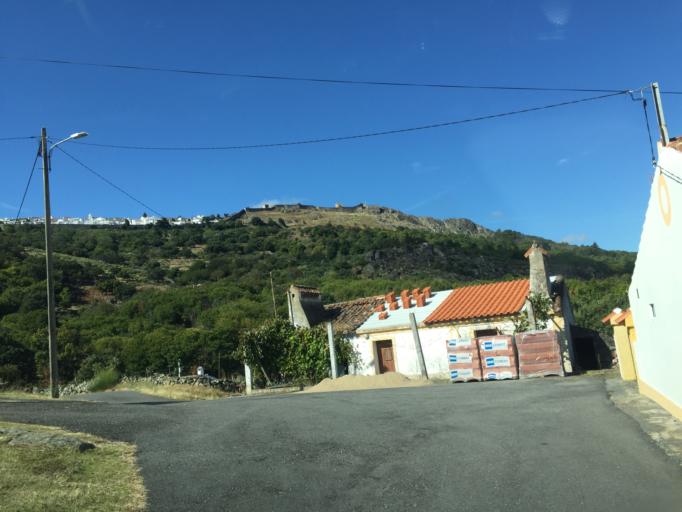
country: PT
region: Portalegre
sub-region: Marvao
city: Marvao
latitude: 39.3985
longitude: -7.3676
